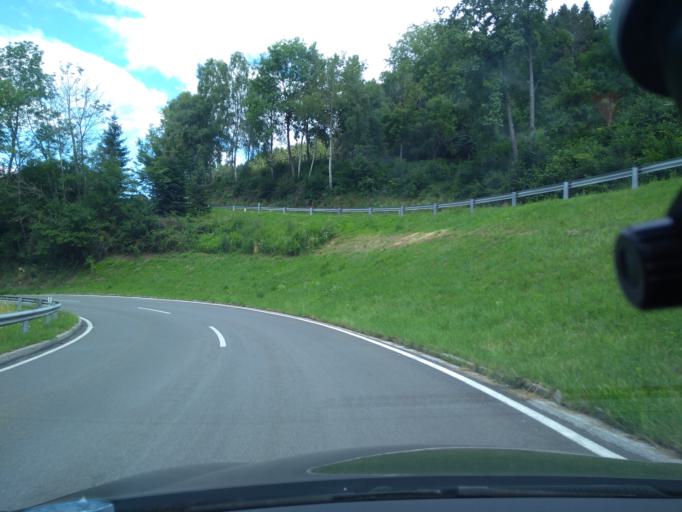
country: AT
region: Styria
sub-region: Politischer Bezirk Graz-Umgebung
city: Semriach
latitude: 47.2206
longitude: 15.4251
